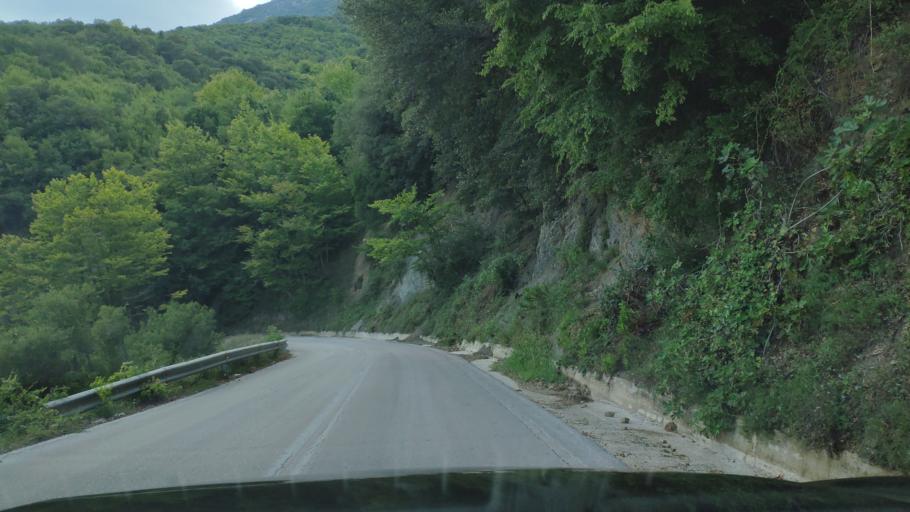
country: GR
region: Epirus
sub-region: Nomos Artas
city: Agios Dimitrios
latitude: 39.4564
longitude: 21.0294
